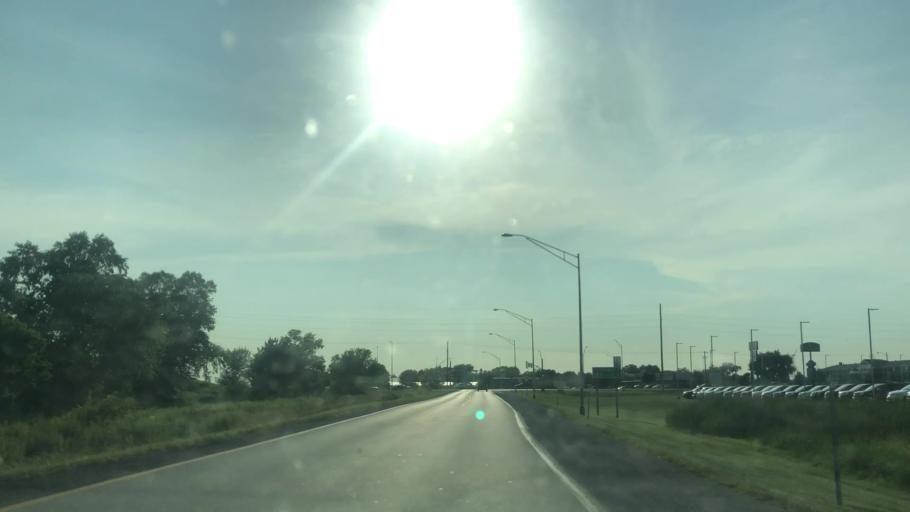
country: US
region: Iowa
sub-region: Story County
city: Ames
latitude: 42.0056
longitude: -93.6073
